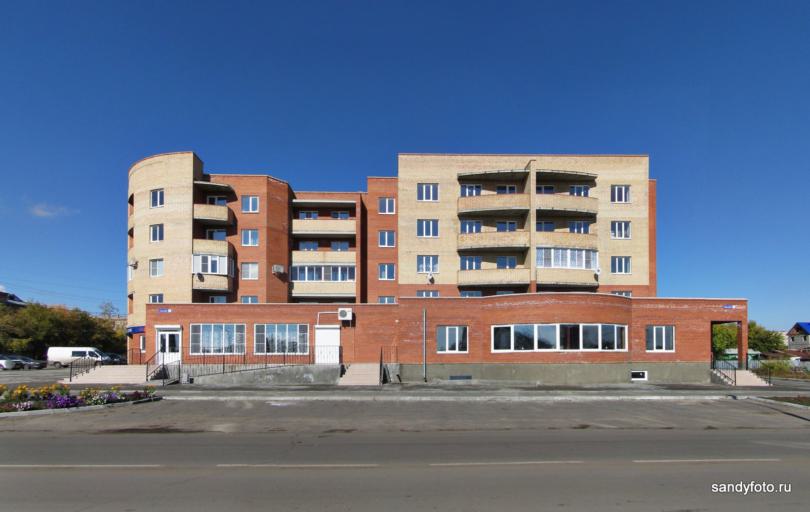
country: RU
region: Chelyabinsk
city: Troitsk
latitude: 54.0771
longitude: 61.5396
